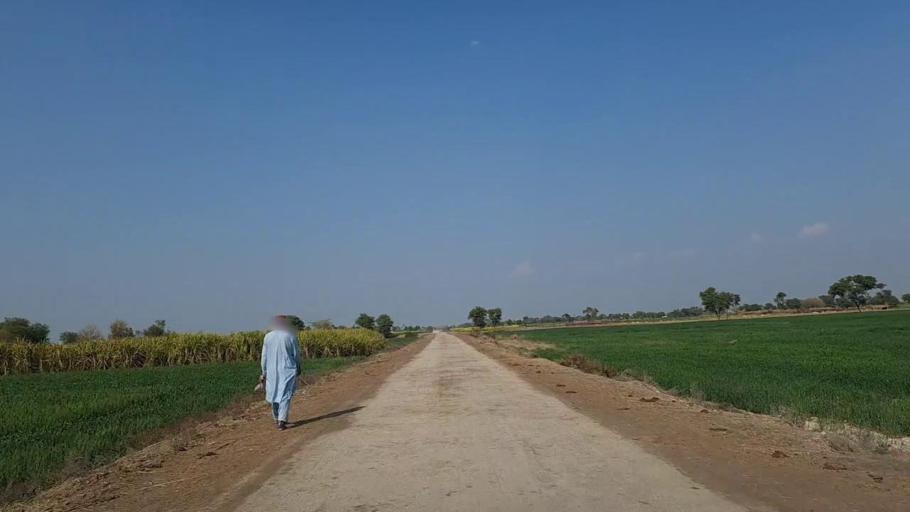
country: PK
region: Sindh
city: Jam Sahib
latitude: 26.2862
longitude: 68.5830
